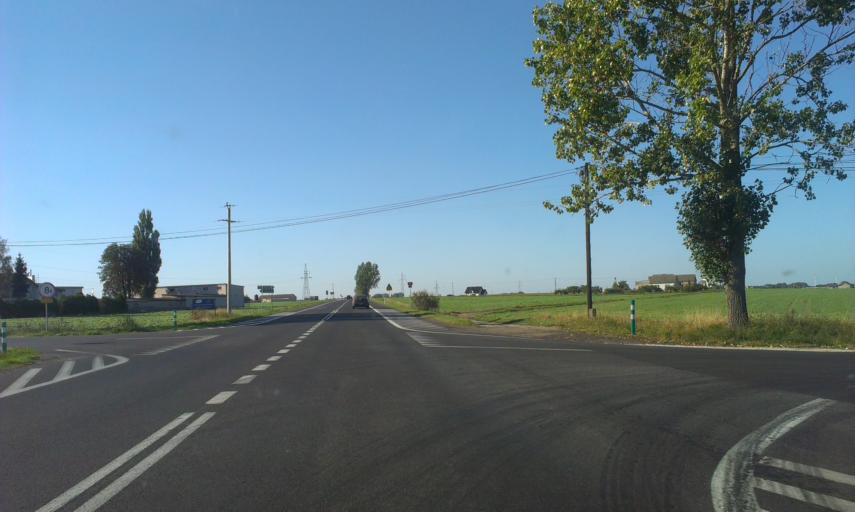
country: PL
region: Kujawsko-Pomorskie
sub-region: Powiat torunski
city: Chelmza
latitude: 53.1547
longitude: 18.6055
